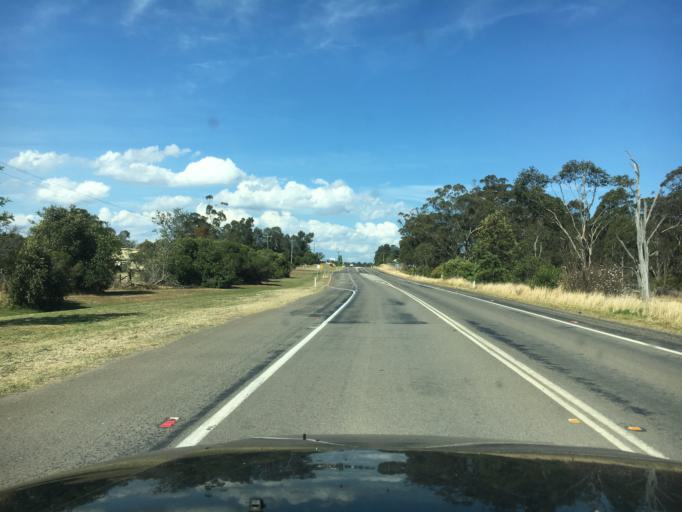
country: AU
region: New South Wales
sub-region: Cessnock
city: Branxton
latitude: -32.6558
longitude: 151.3426
